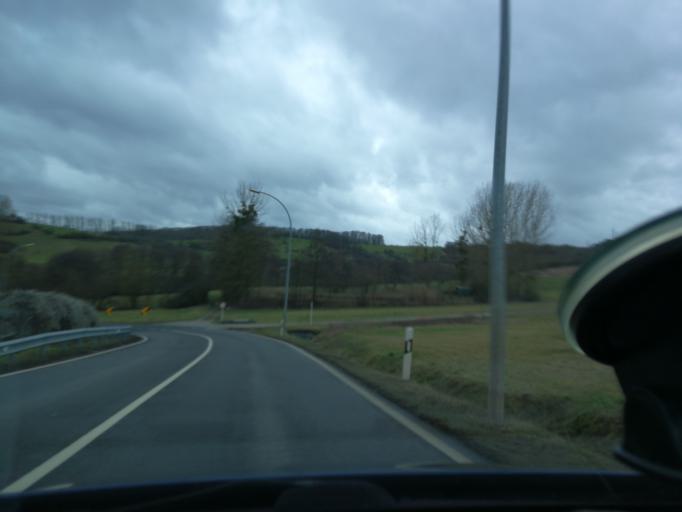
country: DE
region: Rheinland-Pfalz
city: Oberbillig
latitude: 49.7249
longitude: 6.4853
